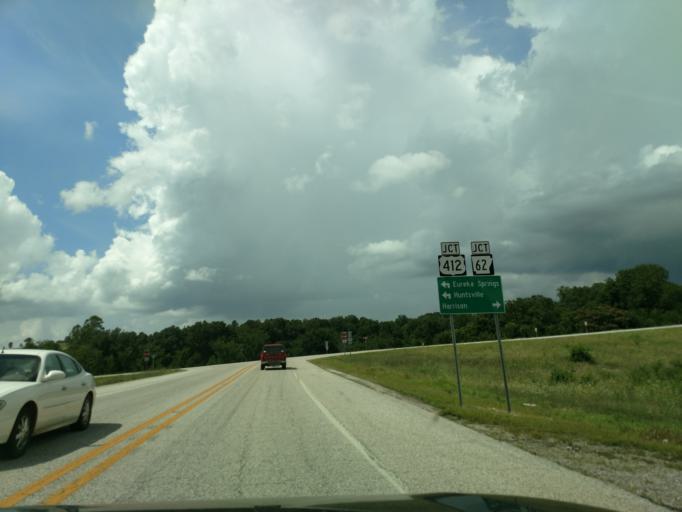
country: US
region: Arkansas
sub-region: Boone County
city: Harrison
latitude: 36.2939
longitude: -93.2423
